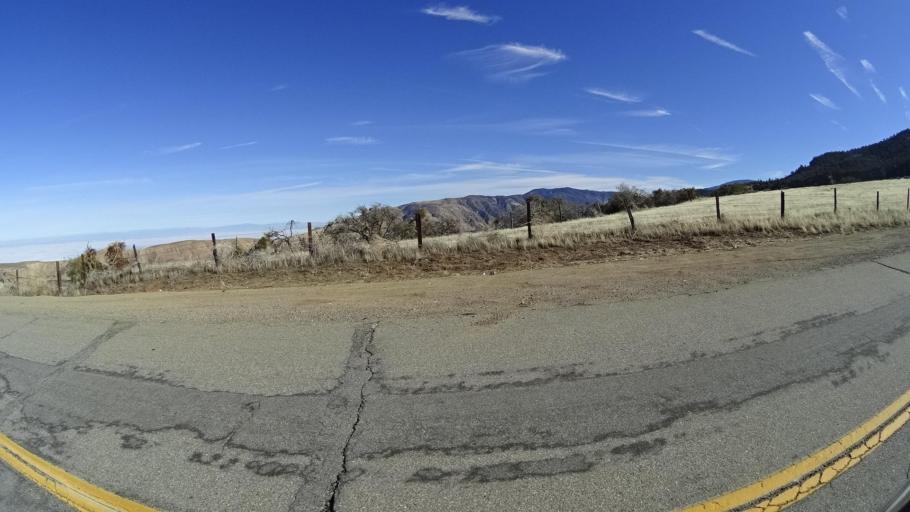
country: US
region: California
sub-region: Kern County
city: Maricopa
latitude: 34.8852
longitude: -119.3531
